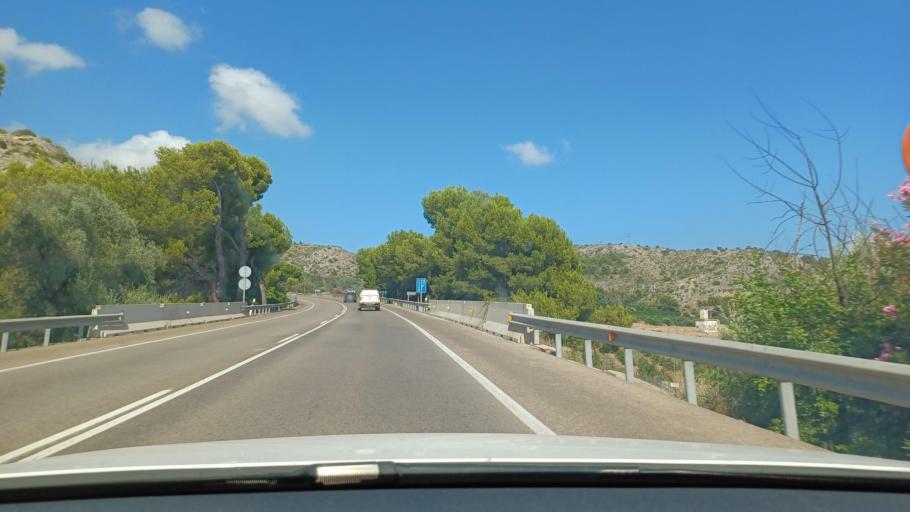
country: ES
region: Valencia
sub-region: Provincia de Castello
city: Benicassim
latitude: 40.0645
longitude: 0.0785
